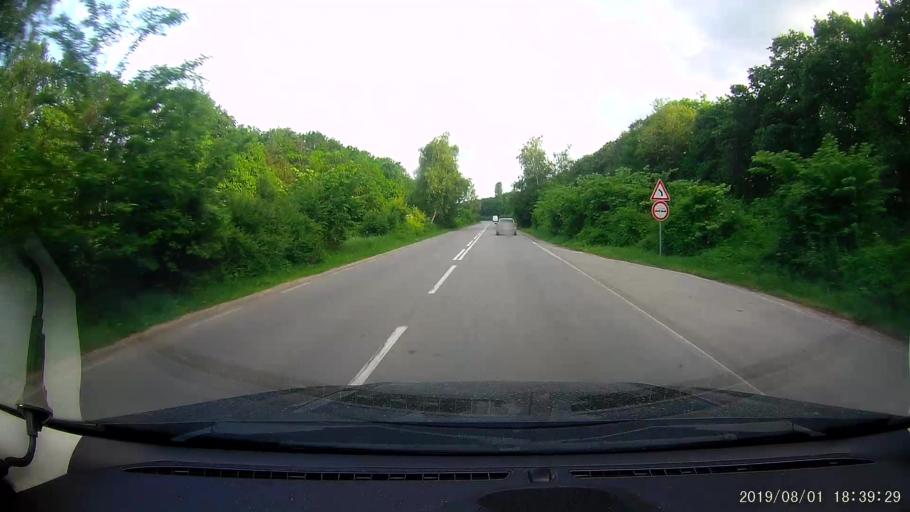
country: BG
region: Shumen
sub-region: Obshtina Khitrino
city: Gara Khitrino
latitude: 43.3848
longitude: 26.9166
